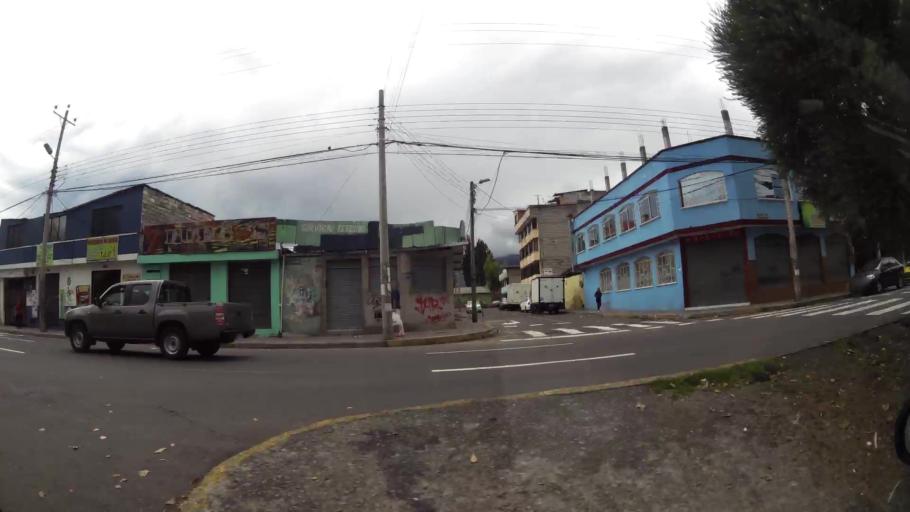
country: EC
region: Pichincha
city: Quito
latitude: -0.2735
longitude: -78.5418
